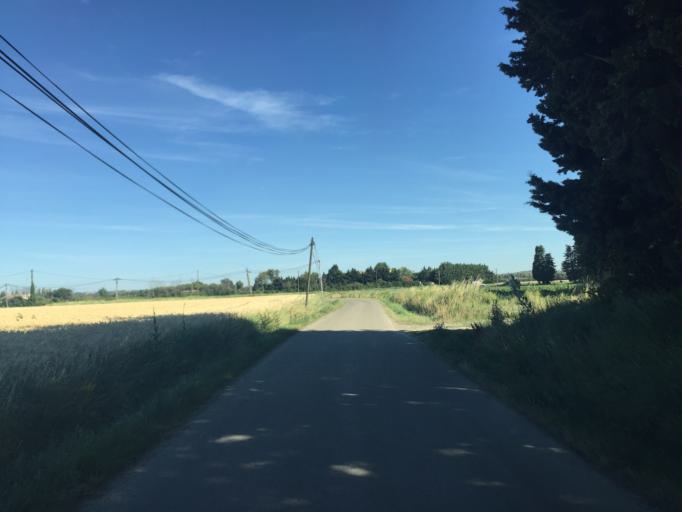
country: FR
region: Provence-Alpes-Cote d'Azur
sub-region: Departement du Vaucluse
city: Caderousse
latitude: 44.1137
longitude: 4.7388
